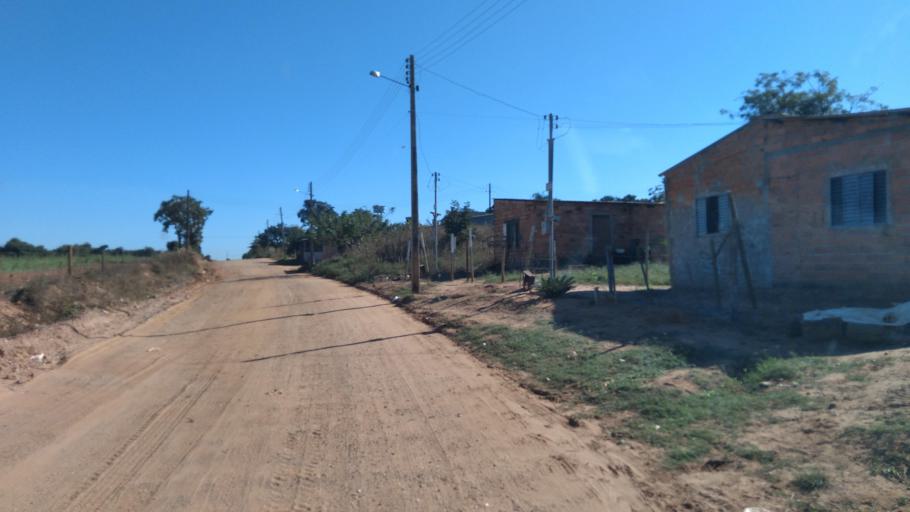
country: BR
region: Goias
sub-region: Mineiros
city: Mineiros
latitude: -17.5948
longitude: -52.5564
